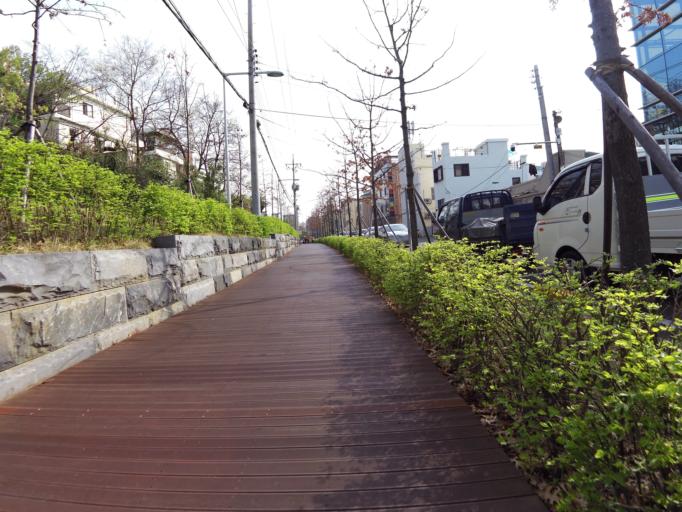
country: KR
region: Daegu
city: Daegu
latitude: 35.8880
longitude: 128.6365
